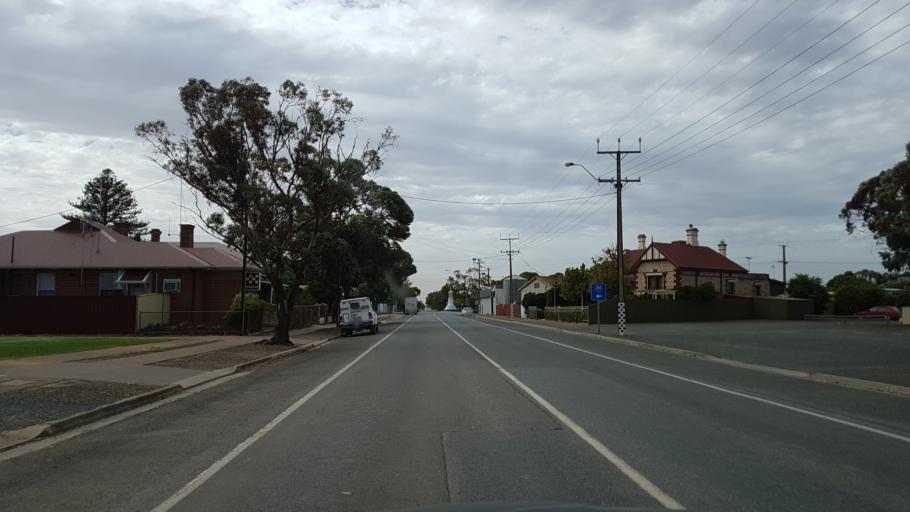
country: AU
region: South Australia
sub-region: Mallala
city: Mallala
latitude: -34.4369
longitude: 138.5079
